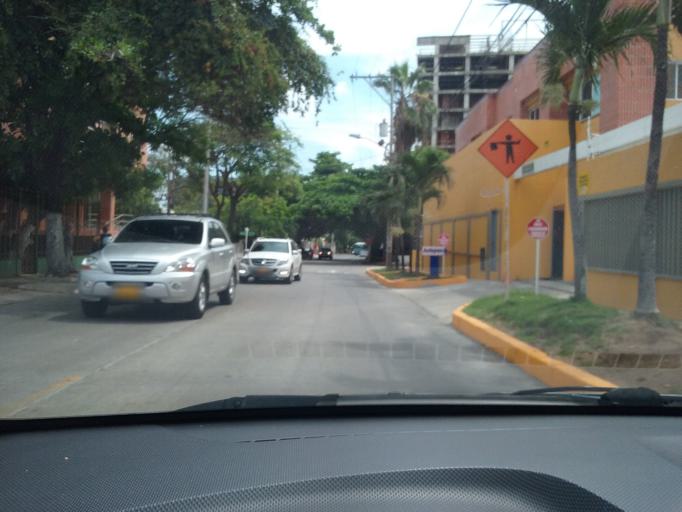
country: CO
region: Atlantico
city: Barranquilla
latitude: 11.0116
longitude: -74.8086
